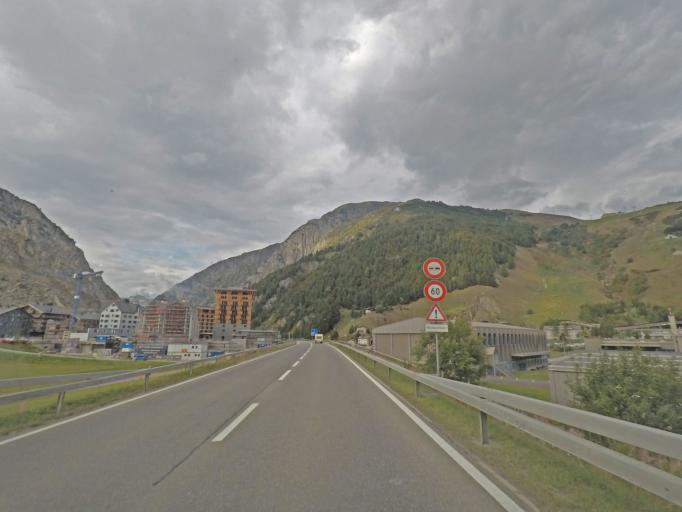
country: CH
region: Uri
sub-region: Uri
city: Andermatt
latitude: 46.6374
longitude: 8.5910
